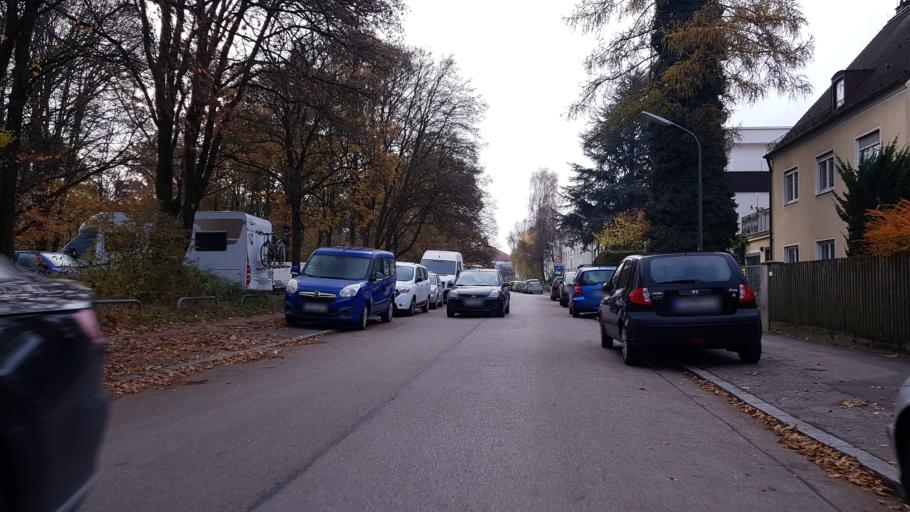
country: DE
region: Bavaria
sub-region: Upper Bavaria
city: Unterhaching
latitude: 48.1069
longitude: 11.6081
